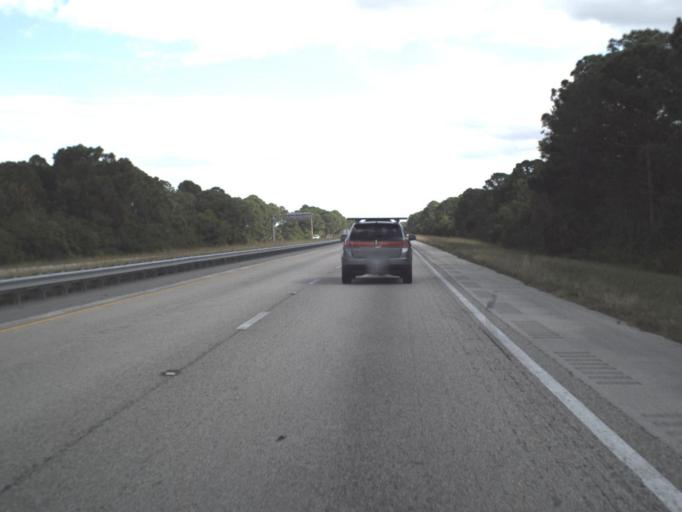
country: US
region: Florida
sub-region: Brevard County
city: Sharpes
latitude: 28.4112
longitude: -80.8063
